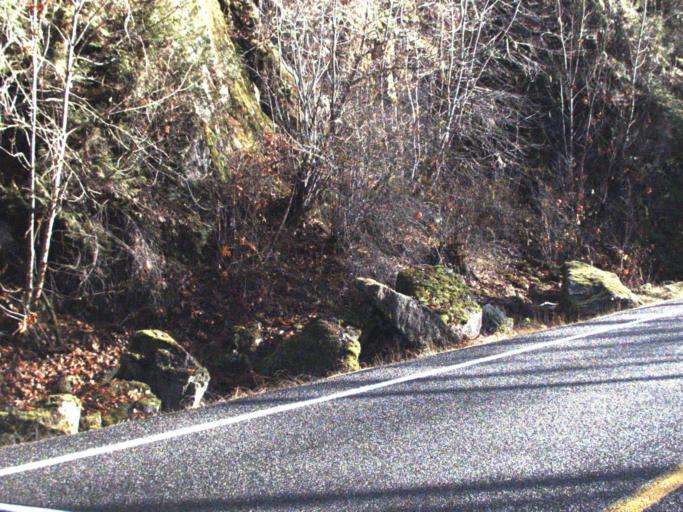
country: US
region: Washington
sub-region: Snohomish County
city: Darrington
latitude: 48.4478
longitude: -121.5852
